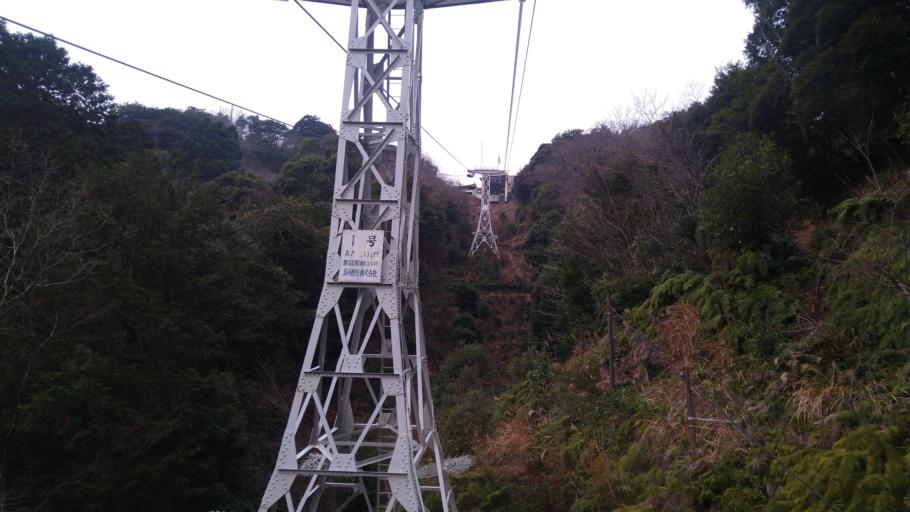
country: JP
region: Hyogo
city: Toyooka
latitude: 35.6237
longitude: 134.7996
